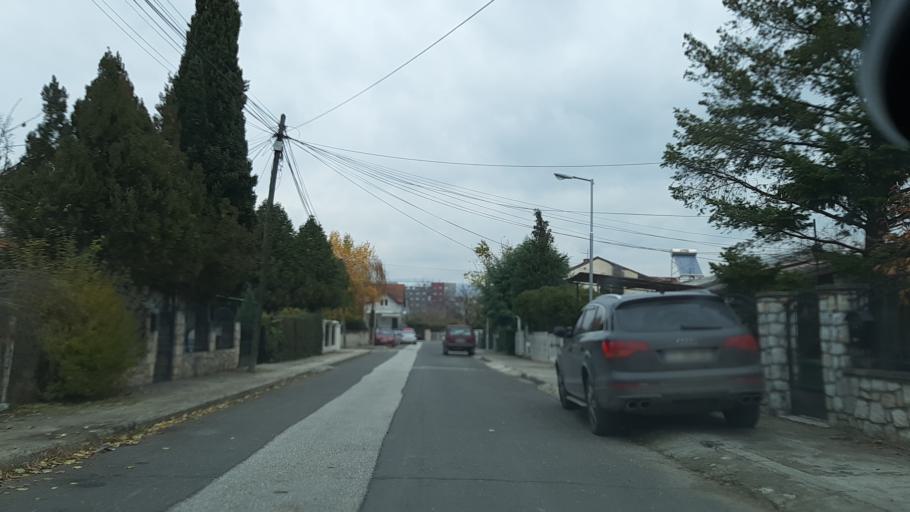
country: MK
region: Kisela Voda
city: Usje
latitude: 41.9772
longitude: 21.4687
